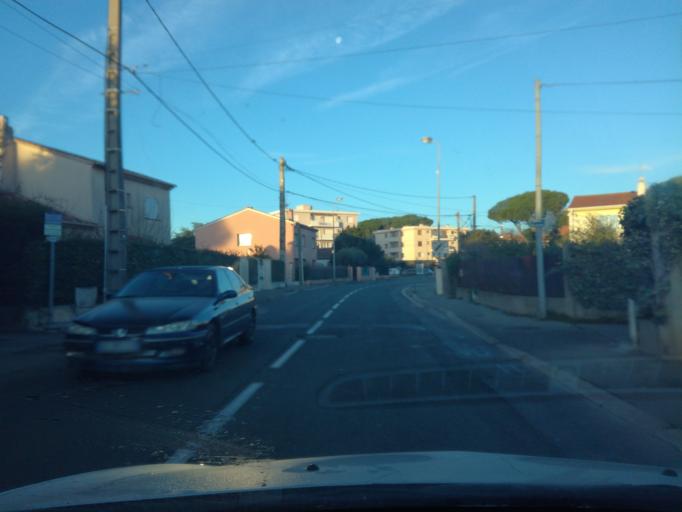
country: FR
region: Provence-Alpes-Cote d'Azur
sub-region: Departement du Var
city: Frejus
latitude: 43.4325
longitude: 6.7432
